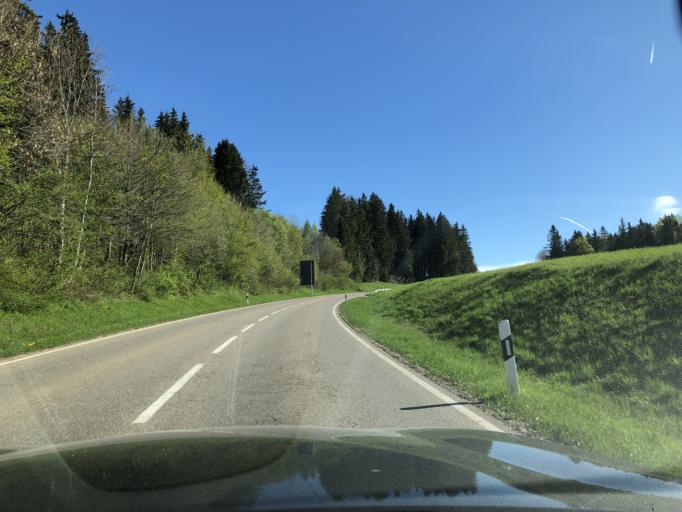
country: DE
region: Bavaria
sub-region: Swabia
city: Ruckholz
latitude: 47.6432
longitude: 10.5292
